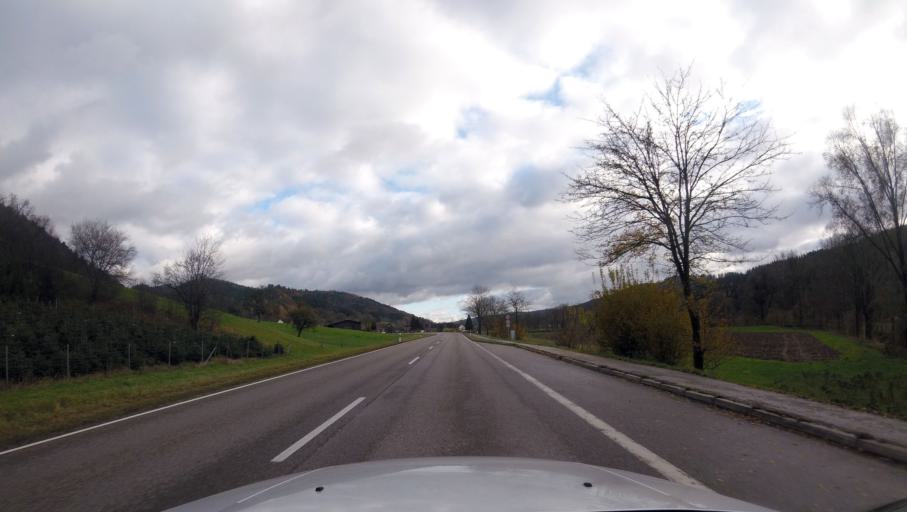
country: DE
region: Baden-Wuerttemberg
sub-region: Regierungsbezirk Stuttgart
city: Sulzbach an der Murr
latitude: 48.9984
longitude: 9.5252
